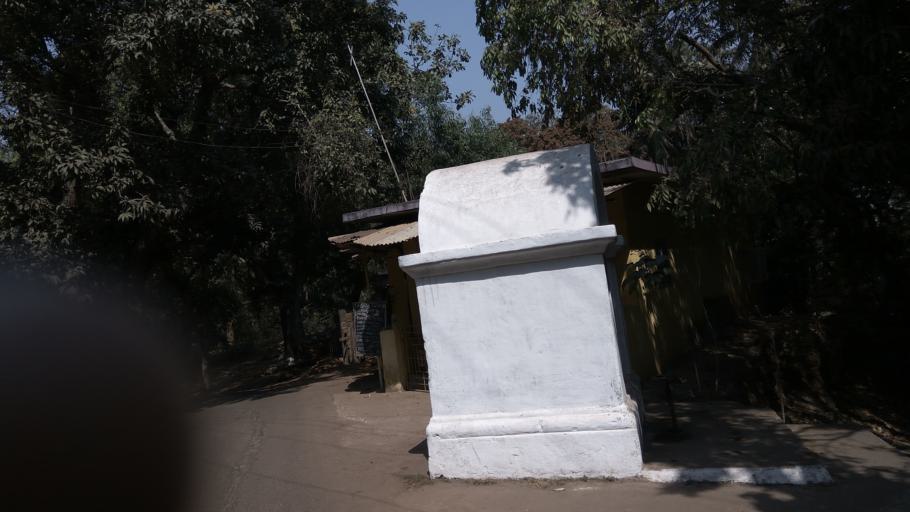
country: IN
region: Goa
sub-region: North Goa
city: Vagator
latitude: 15.6012
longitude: 73.7394
